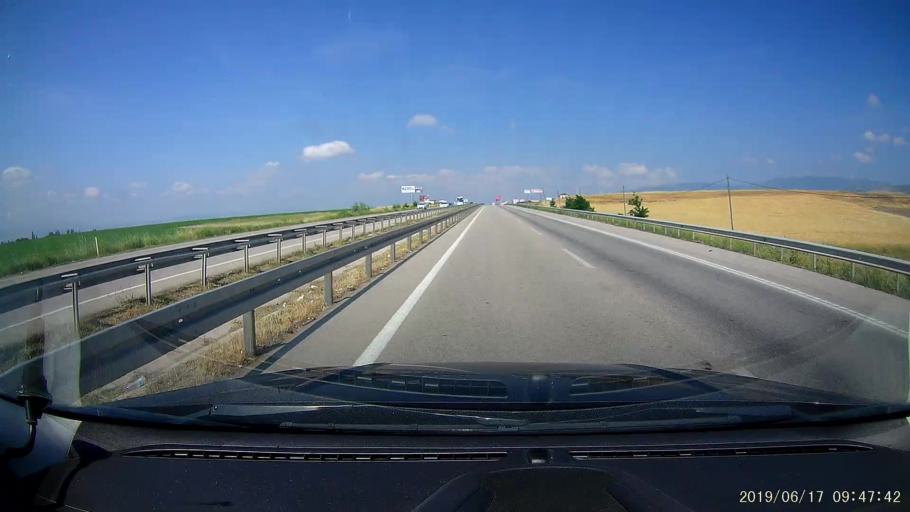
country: TR
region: Amasya
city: Suluova
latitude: 40.8760
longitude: 35.5721
